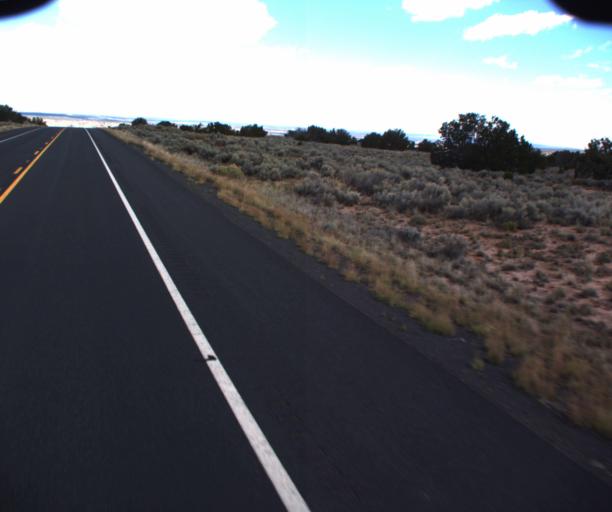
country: US
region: Arizona
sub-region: Apache County
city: Houck
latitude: 35.1740
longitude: -109.3381
